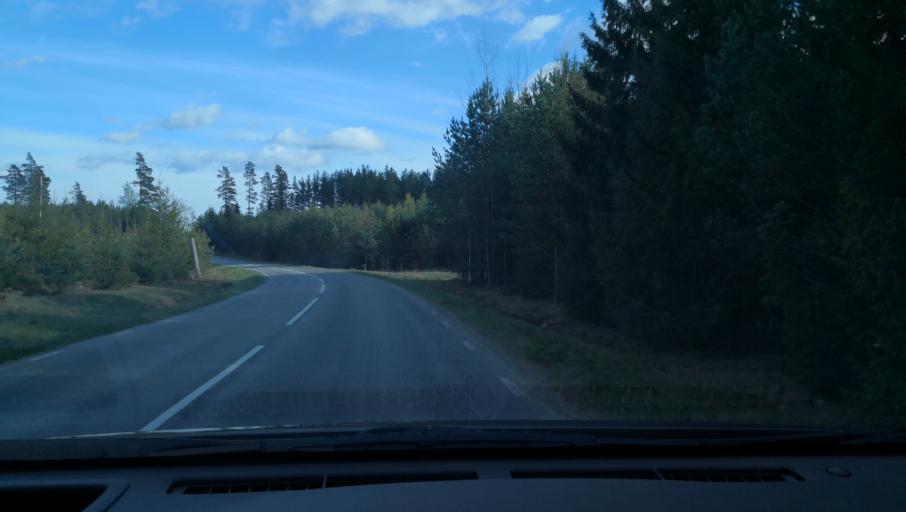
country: SE
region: OErebro
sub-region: Askersunds Kommun
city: Asbro
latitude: 58.9020
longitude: 15.1018
